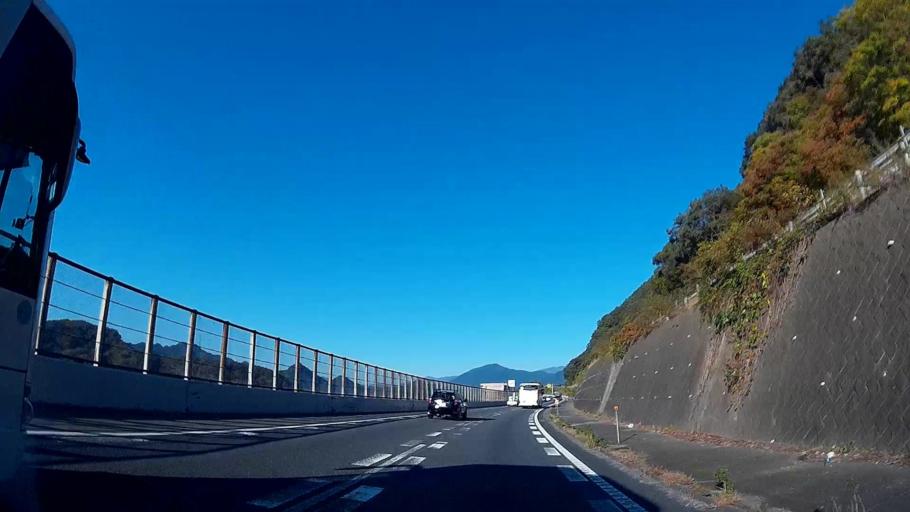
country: JP
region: Yamanashi
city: Uenohara
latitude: 35.6165
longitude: 139.1488
